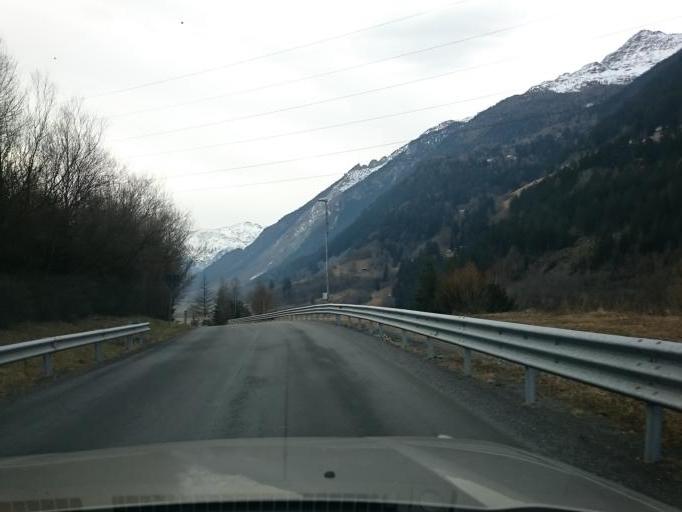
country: IT
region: Lombardy
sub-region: Provincia di Sondrio
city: Valdisotto
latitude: 46.4079
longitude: 10.3508
